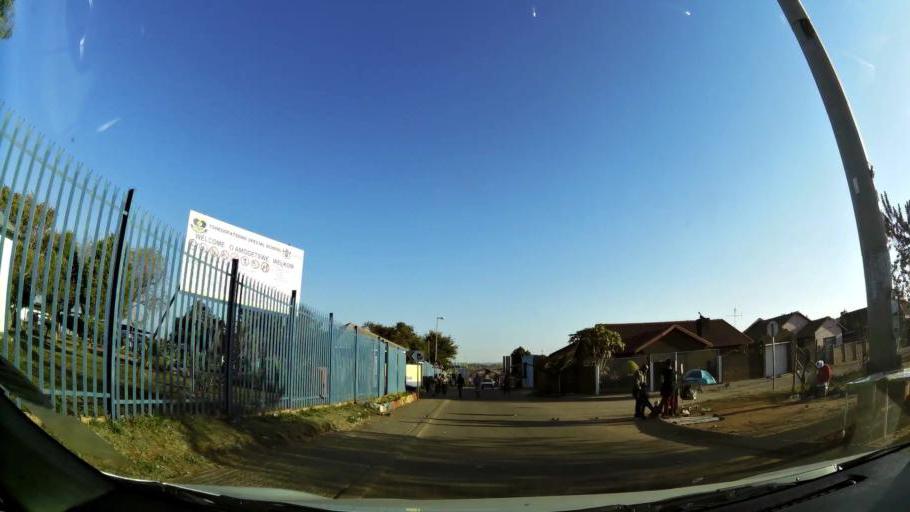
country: ZA
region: Gauteng
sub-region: City of Tshwane Metropolitan Municipality
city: Cullinan
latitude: -25.7257
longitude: 28.3858
